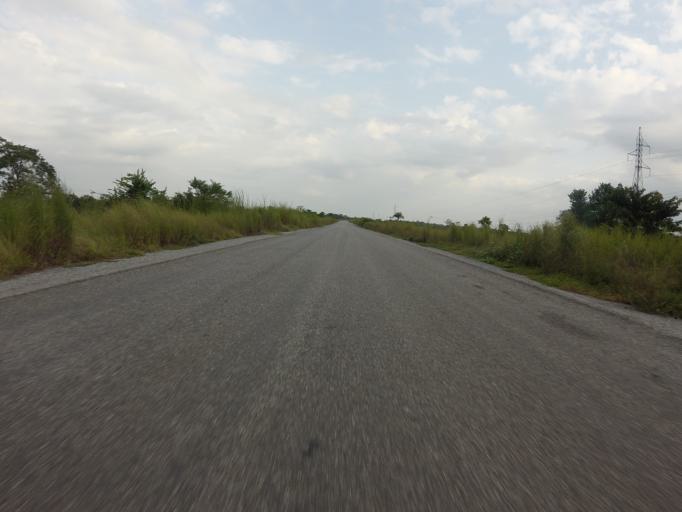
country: GH
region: Volta
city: Ho
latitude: 6.4087
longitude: 0.5227
